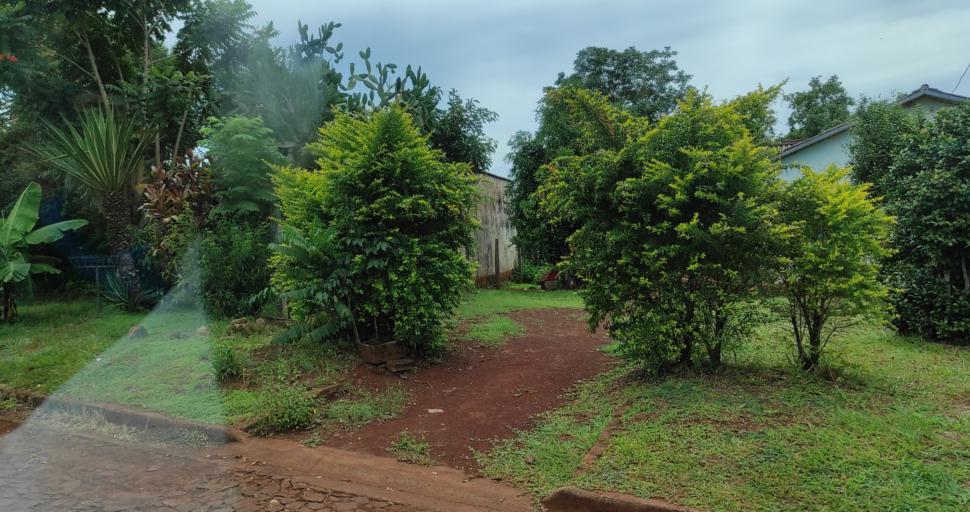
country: AR
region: Misiones
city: El Alcazar
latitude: -26.7181
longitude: -54.8136
